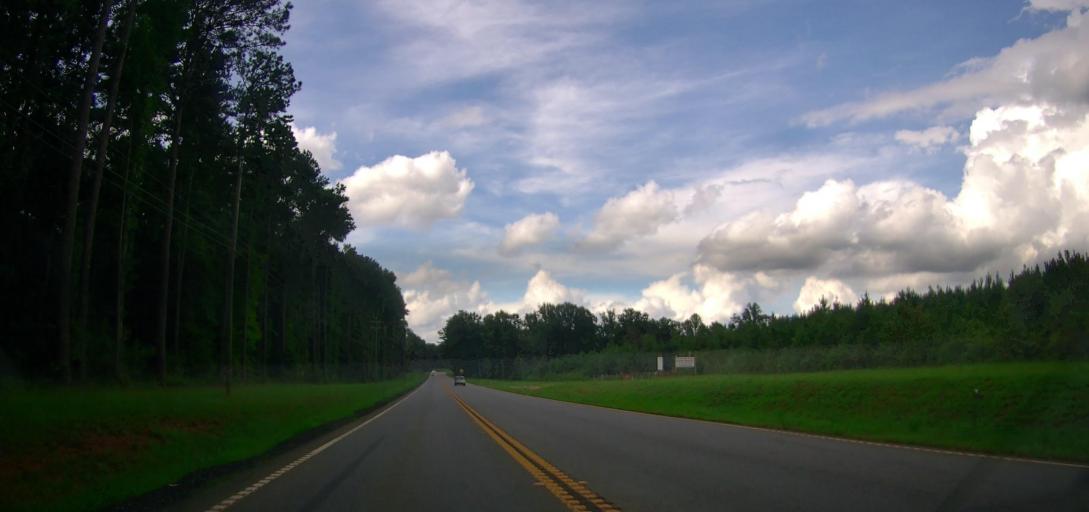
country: US
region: Georgia
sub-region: Harris County
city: Hamilton
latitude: 32.7255
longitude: -84.8743
